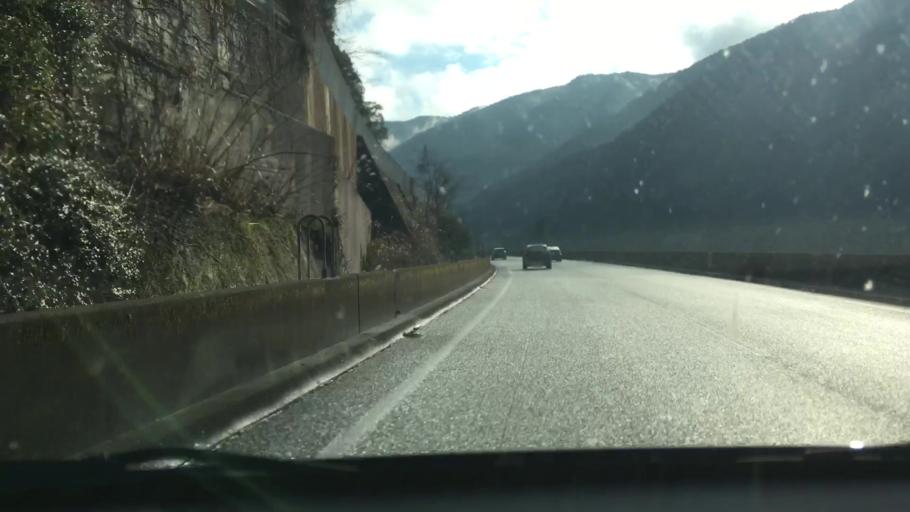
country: JP
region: Kumamoto
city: Yatsushiro
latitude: 32.4146
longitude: 130.6957
